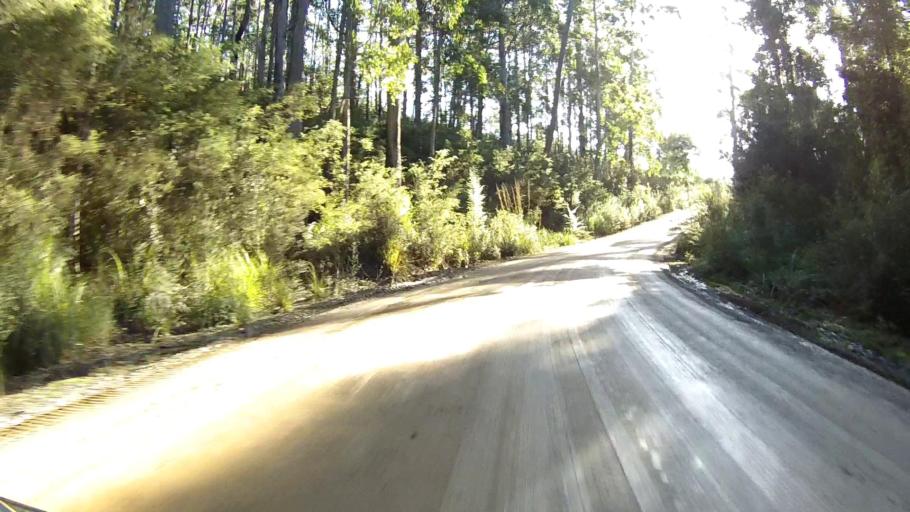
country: AU
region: Tasmania
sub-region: Clarence
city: Sandford
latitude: -43.1194
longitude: 147.9217
